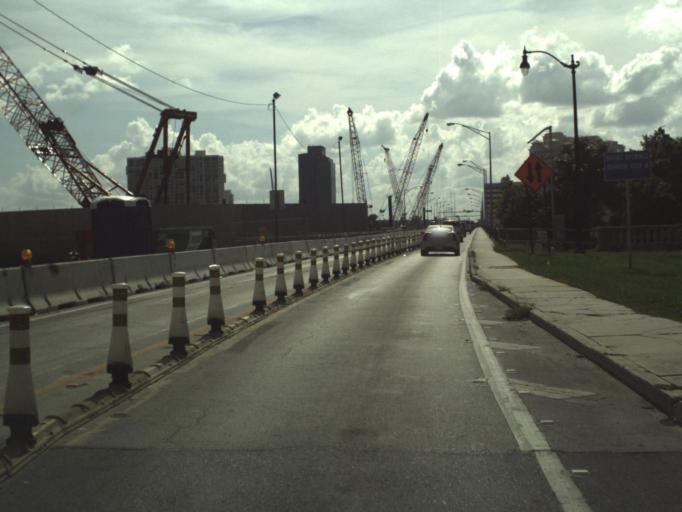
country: US
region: Florida
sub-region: Palm Beach County
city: West Palm Beach
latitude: 26.7182
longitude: -80.0429
